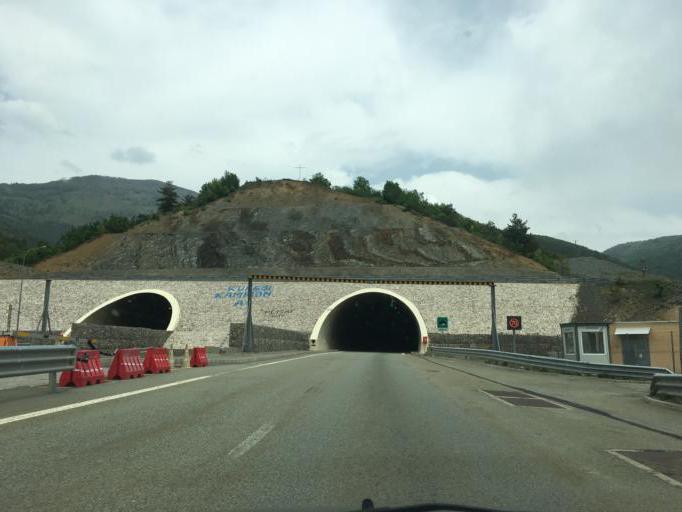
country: AL
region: Lezhe
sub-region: Rrethi i Lezhes
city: Shengjin
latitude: 42.0037
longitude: 20.2280
